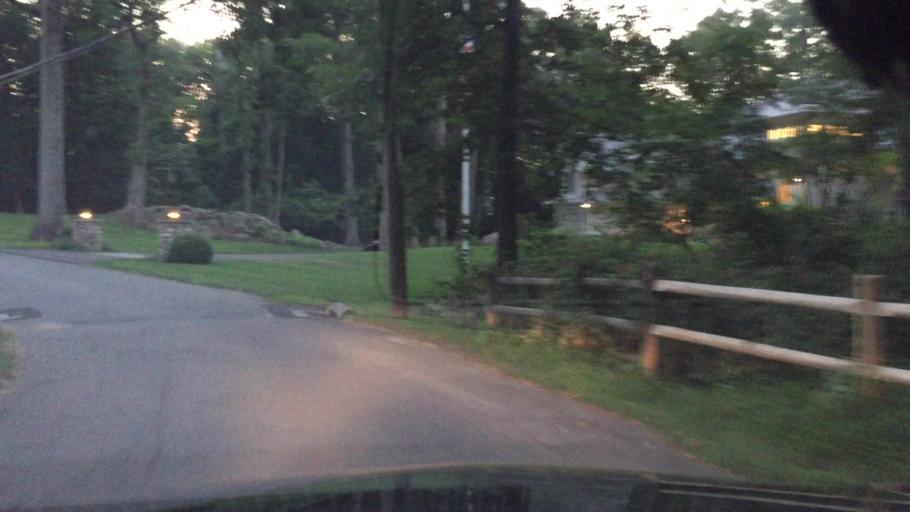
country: US
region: Connecticut
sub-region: Fairfield County
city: East Norwalk
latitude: 41.0761
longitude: -73.4228
